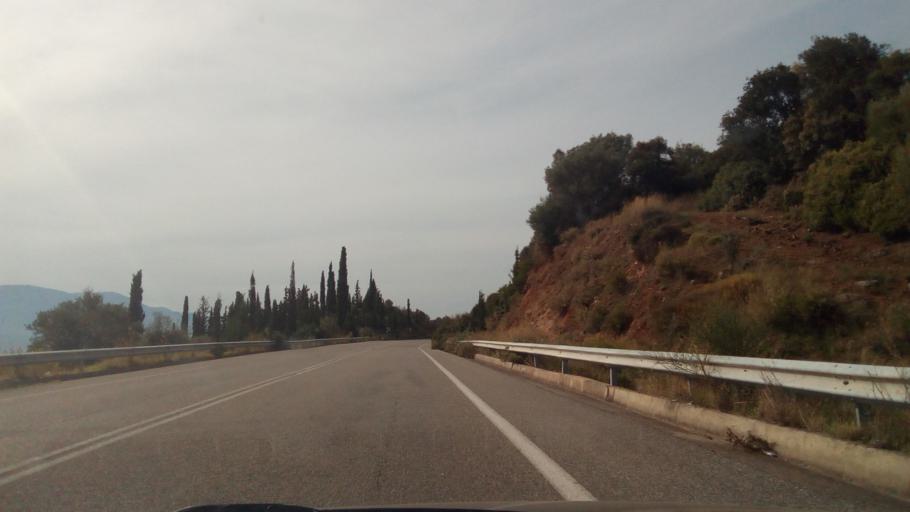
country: GR
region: West Greece
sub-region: Nomos Aitolias kai Akarnanias
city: Nafpaktos
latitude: 38.3875
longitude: 21.7964
